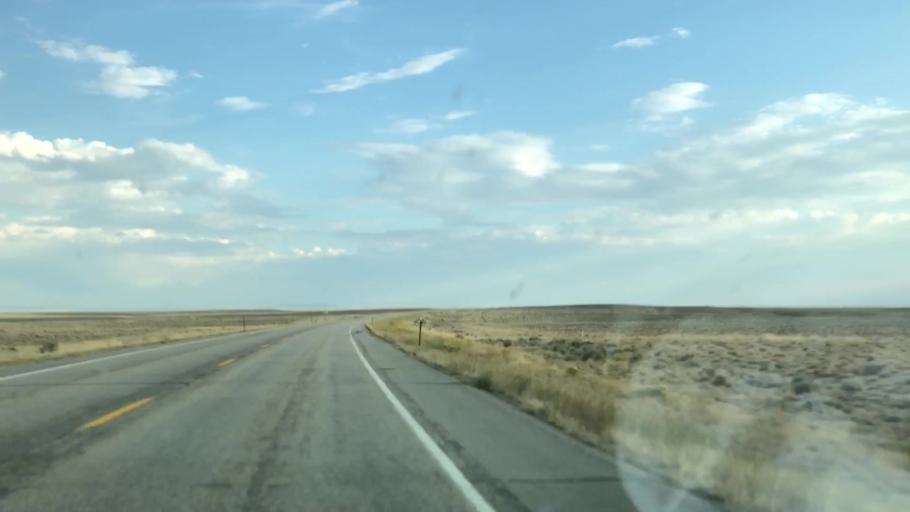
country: US
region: Wyoming
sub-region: Sweetwater County
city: North Rock Springs
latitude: 42.2574
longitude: -109.4698
